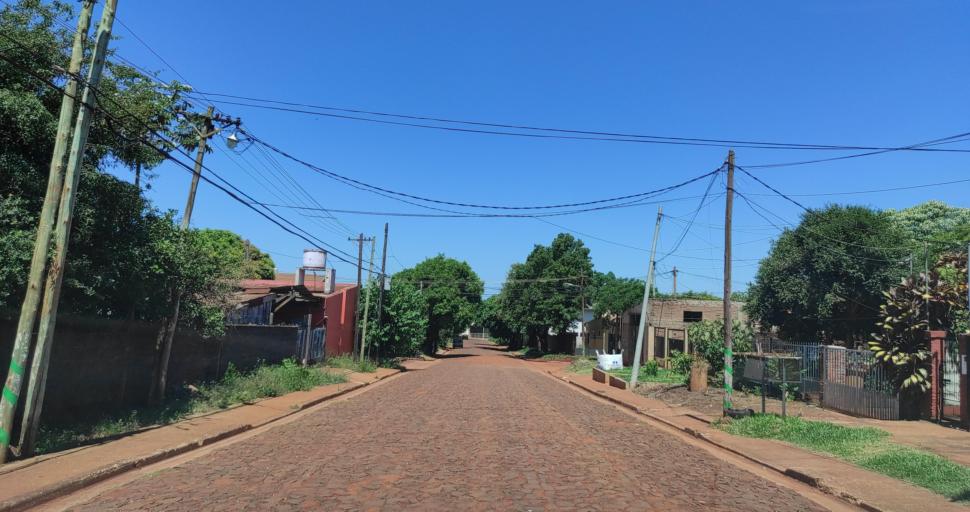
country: AR
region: Misiones
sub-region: Departamento de Capital
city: Posadas
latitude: -27.4050
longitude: -55.9136
